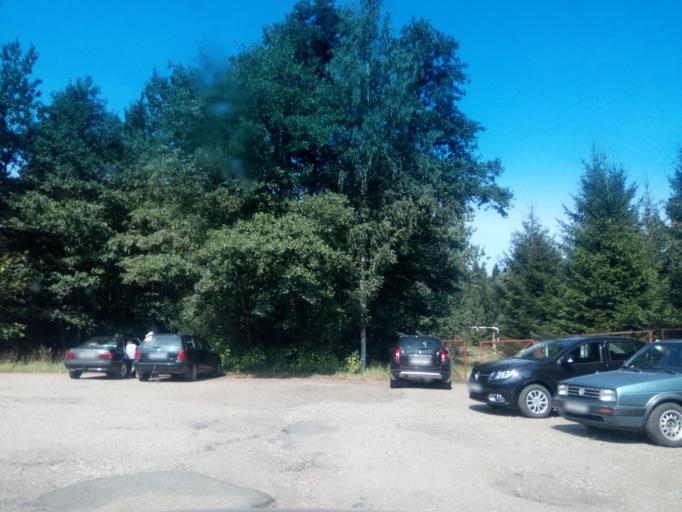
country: BY
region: Vitebsk
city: Vyerkhnyadzvinsk
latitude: 55.7981
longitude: 27.9550
